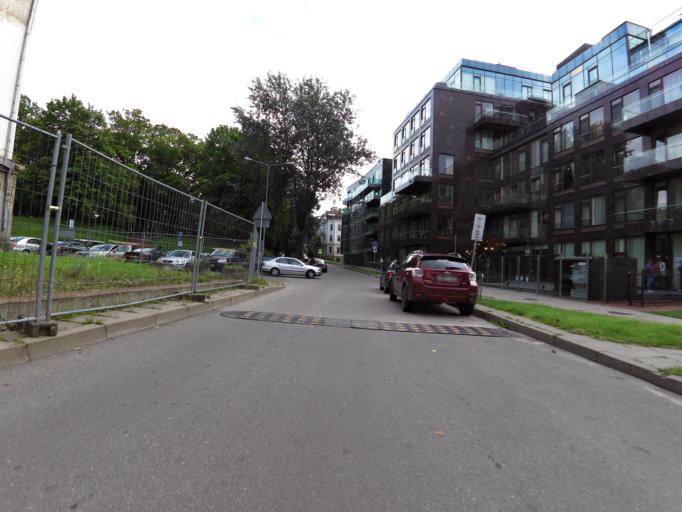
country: LT
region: Vilnius County
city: Naujamiestis
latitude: 54.6852
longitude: 25.2681
